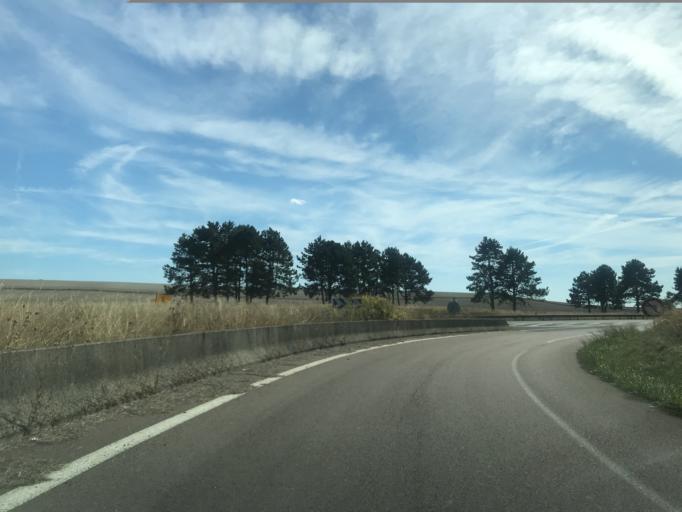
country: FR
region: Champagne-Ardenne
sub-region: Departement de la Marne
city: Chatillon-sur-Marne
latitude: 49.1581
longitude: 3.7202
